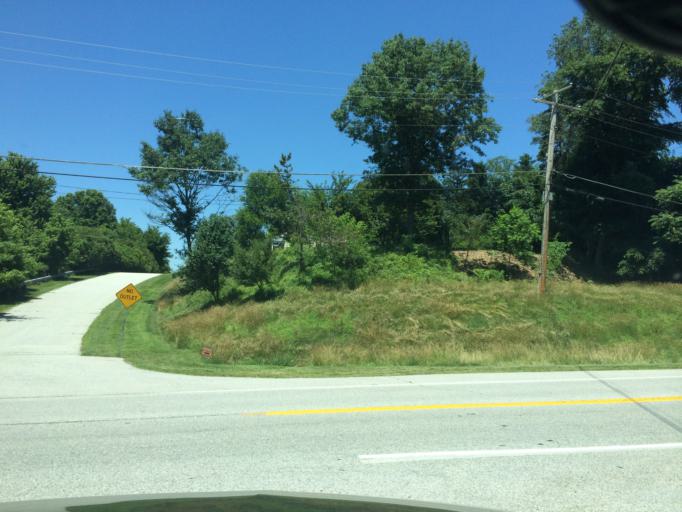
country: US
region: Maryland
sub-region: Baltimore County
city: Garrison
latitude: 39.3909
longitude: -76.7617
